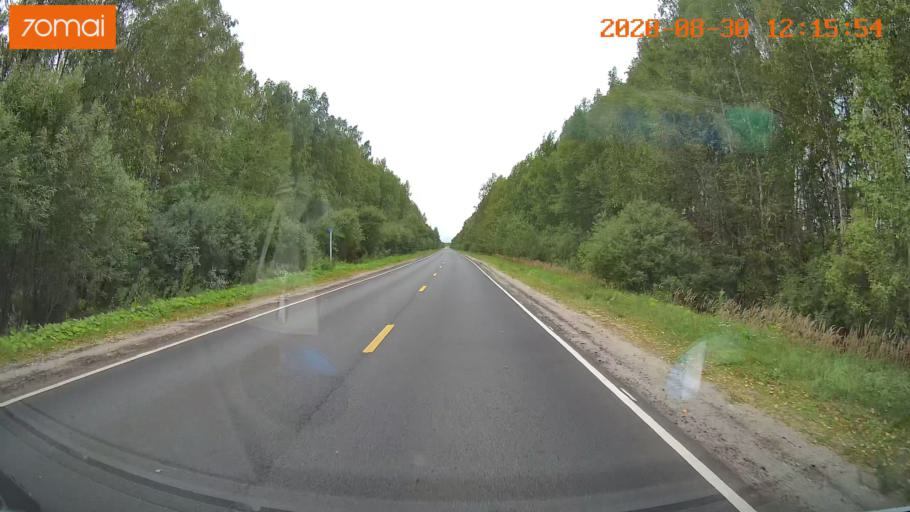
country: RU
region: Ivanovo
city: Yur'yevets
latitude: 57.3189
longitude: 43.0179
